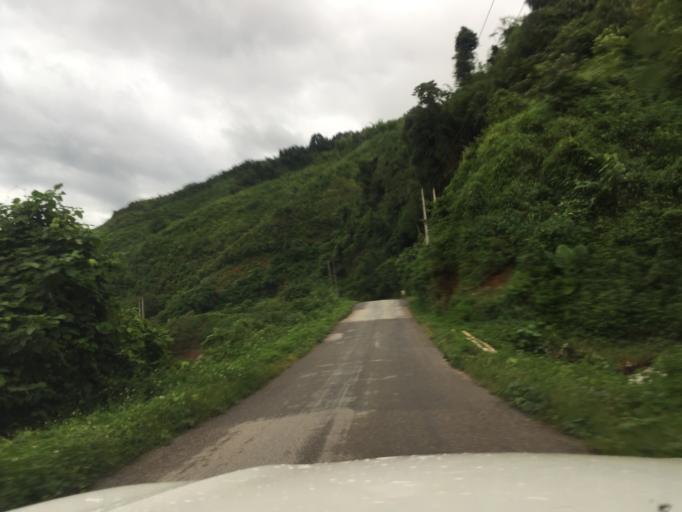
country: LA
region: Oudomxai
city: Muang La
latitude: 20.9790
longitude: 102.2240
